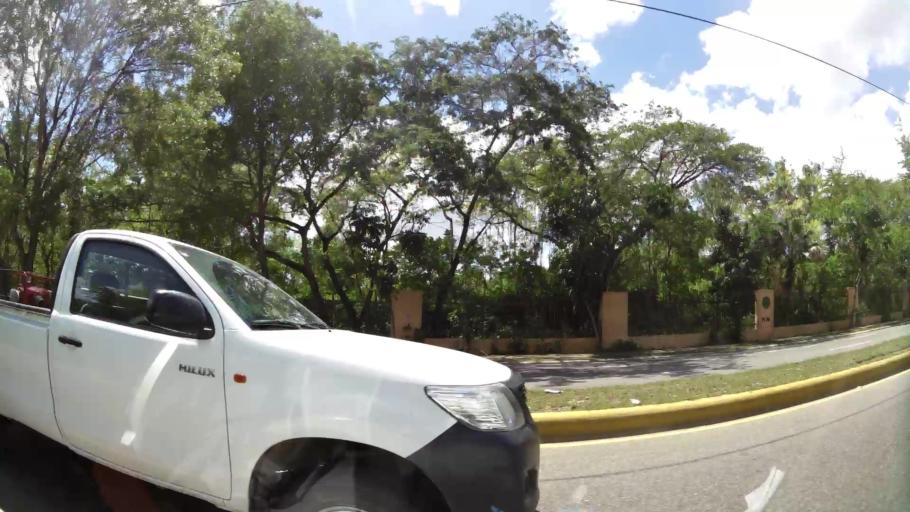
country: DO
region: Nacional
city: La Agustina
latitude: 18.5188
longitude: -69.9192
